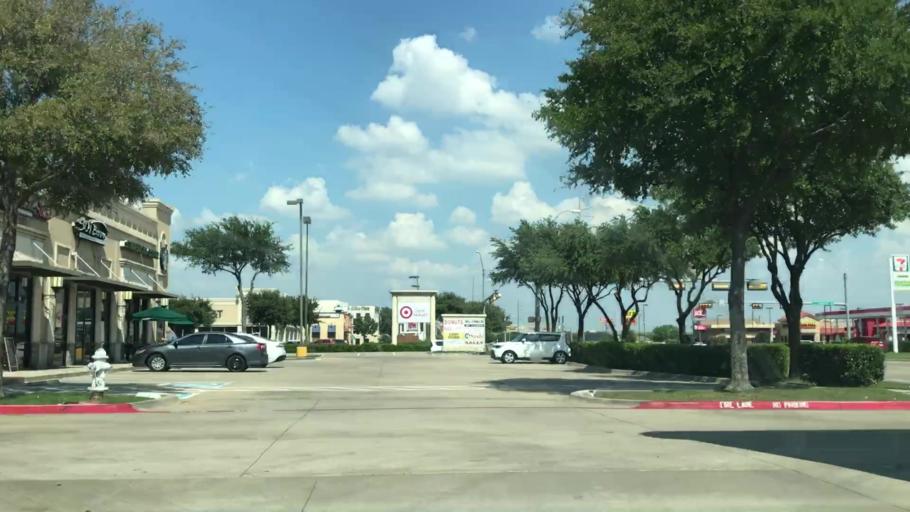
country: US
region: Texas
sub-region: Denton County
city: Lewisville
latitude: 33.0097
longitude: -96.9695
